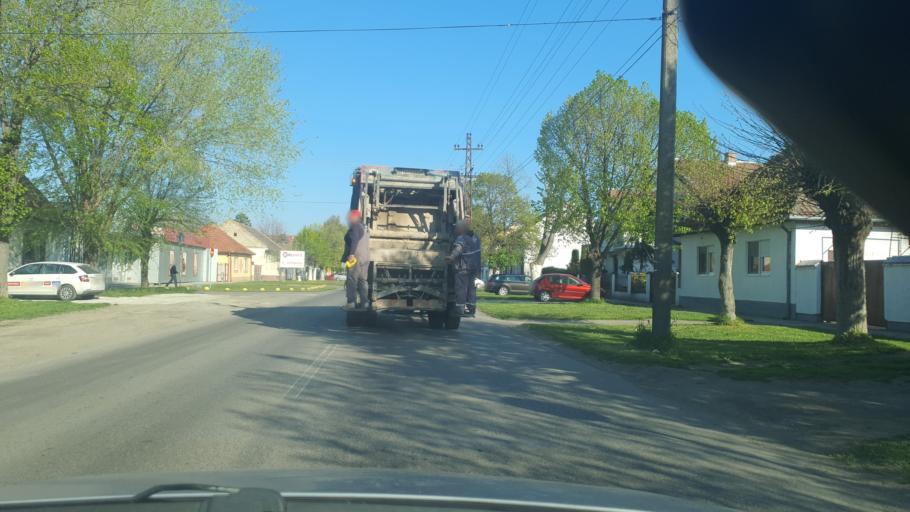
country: RS
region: Autonomna Pokrajina Vojvodina
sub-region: Juznobacki Okrug
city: Vrbas
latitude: 45.5651
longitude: 19.6523
